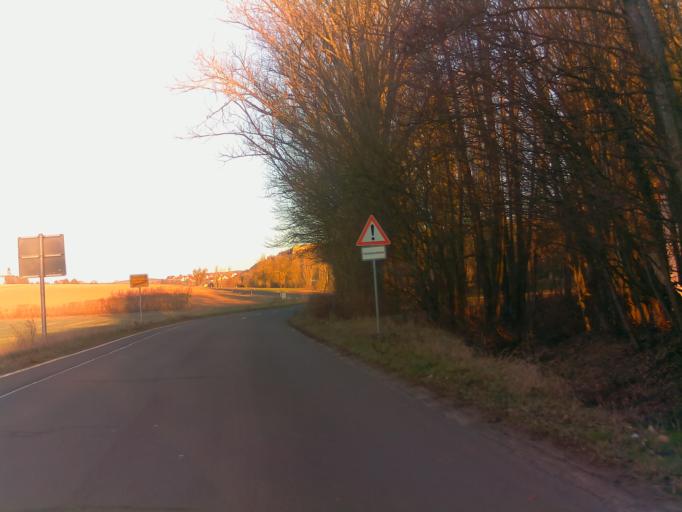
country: DE
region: Rheinland-Pfalz
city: Marnheim
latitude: 49.6340
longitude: 8.0275
